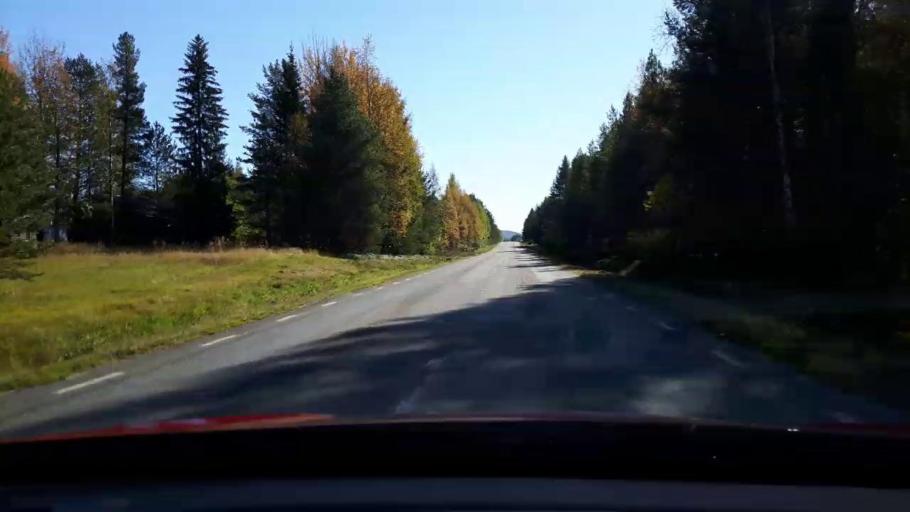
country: SE
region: Jaemtland
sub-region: Harjedalens Kommun
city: Sveg
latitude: 62.3085
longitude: 14.0440
